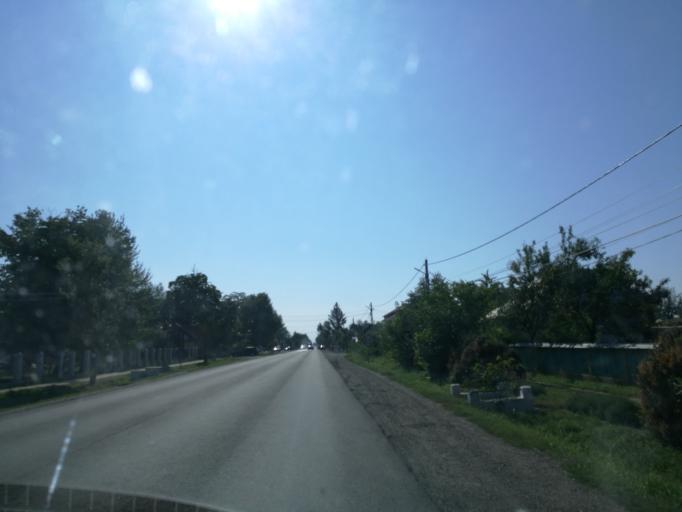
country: RO
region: Suceava
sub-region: Comuna Vadu Moldovei
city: Vadu Moldovei
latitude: 47.3778
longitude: 26.3692
